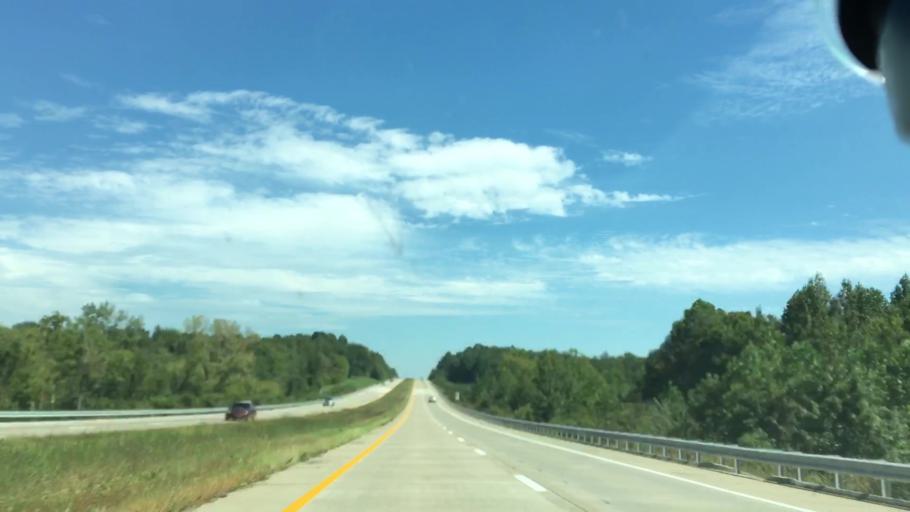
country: US
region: Indiana
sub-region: Warrick County
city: Newburgh
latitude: 37.7532
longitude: -87.3766
